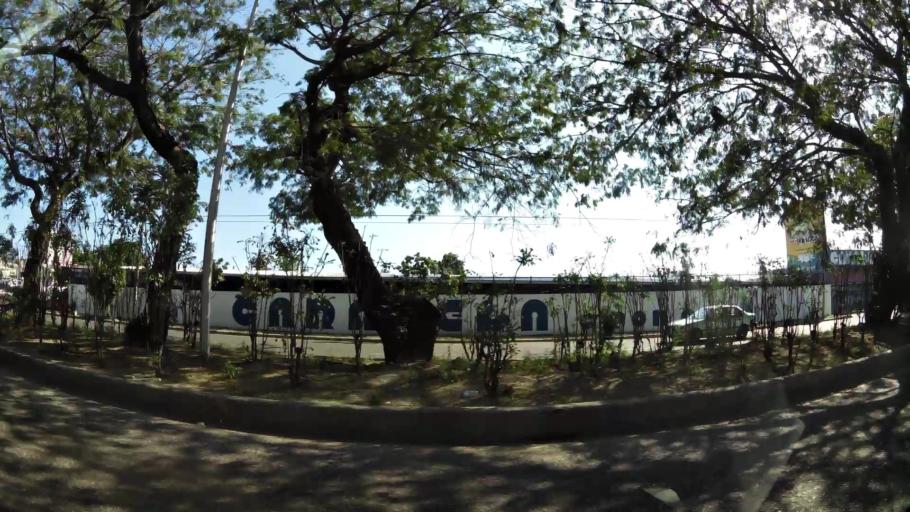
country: DO
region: San Cristobal
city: El Carril
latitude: 18.4608
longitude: -69.9912
